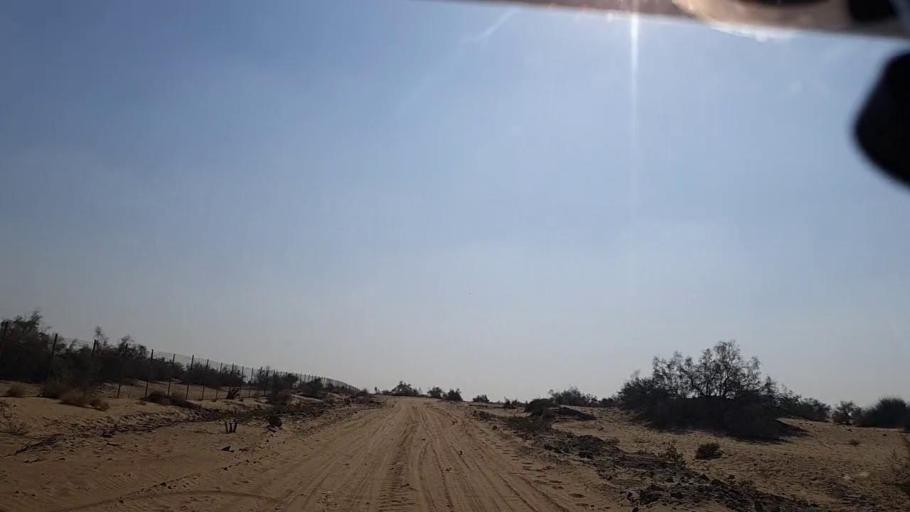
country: PK
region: Sindh
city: Khanpur
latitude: 27.5610
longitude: 69.3886
